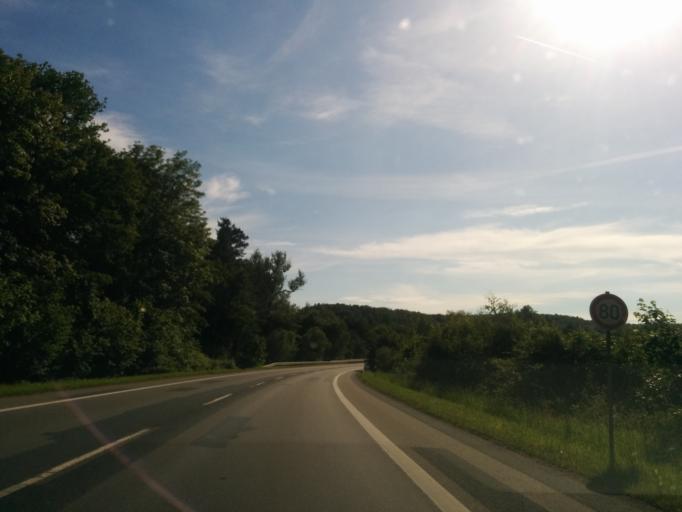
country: DE
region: Lower Saxony
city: Elbingerode
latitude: 51.6285
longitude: 10.2741
